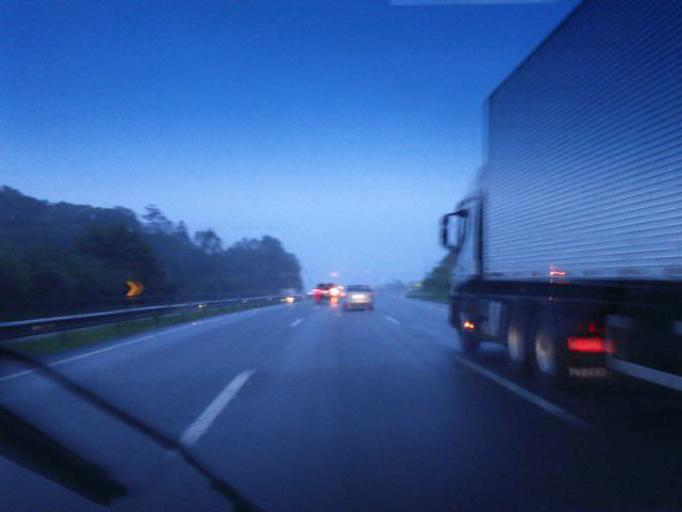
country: BR
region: Sao Paulo
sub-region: Juquitiba
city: Juquitiba
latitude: -23.9861
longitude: -47.1480
